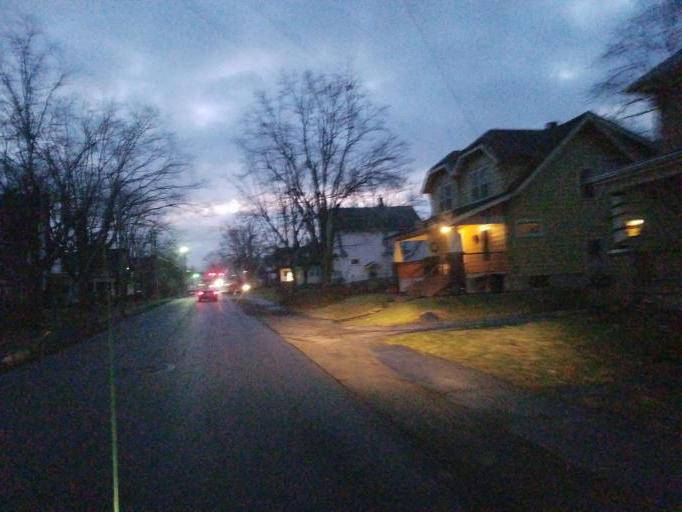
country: US
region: Ohio
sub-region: Marion County
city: Marion
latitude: 40.5768
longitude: -83.1336
